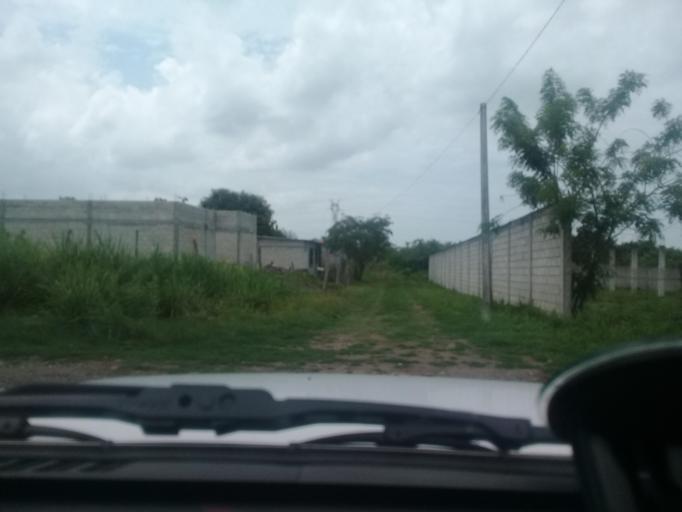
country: MX
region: Veracruz
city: Paso de Ovejas
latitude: 19.2932
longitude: -96.4400
